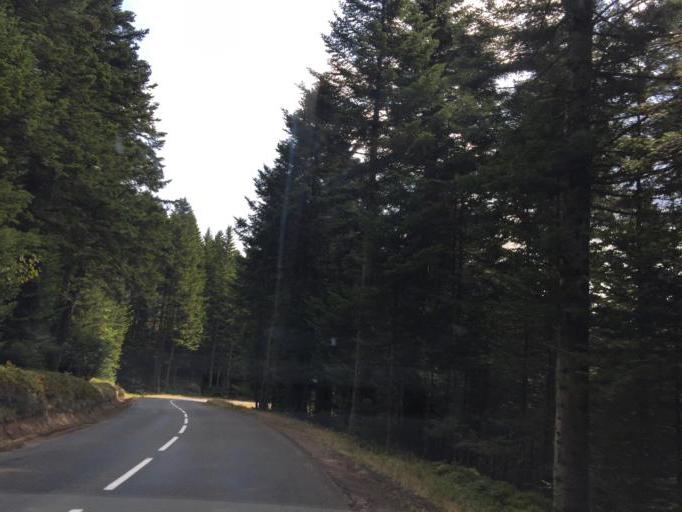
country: FR
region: Rhone-Alpes
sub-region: Departement de la Loire
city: Bourg-Argental
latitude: 45.3726
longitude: 4.5457
